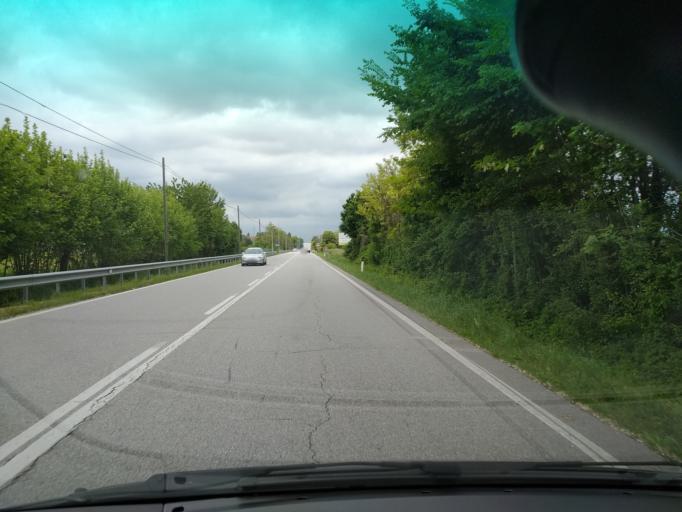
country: IT
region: Veneto
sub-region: Provincia di Padova
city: Curtarolo
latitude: 45.4988
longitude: 11.8257
